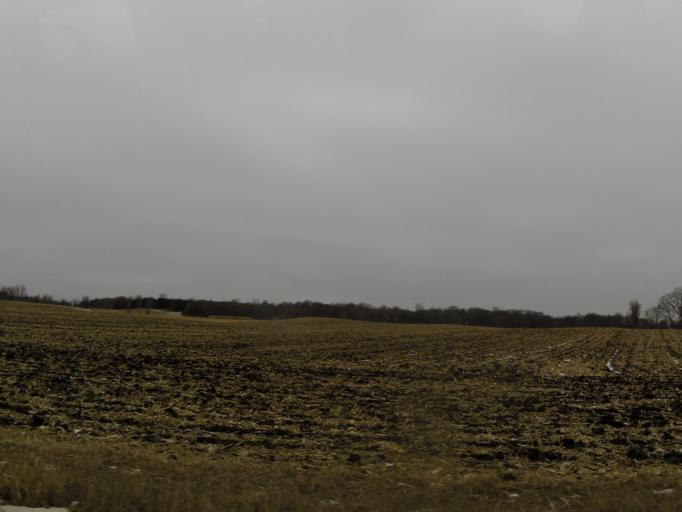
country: US
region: Minnesota
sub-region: Carver County
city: Watertown
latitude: 45.0209
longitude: -93.8499
